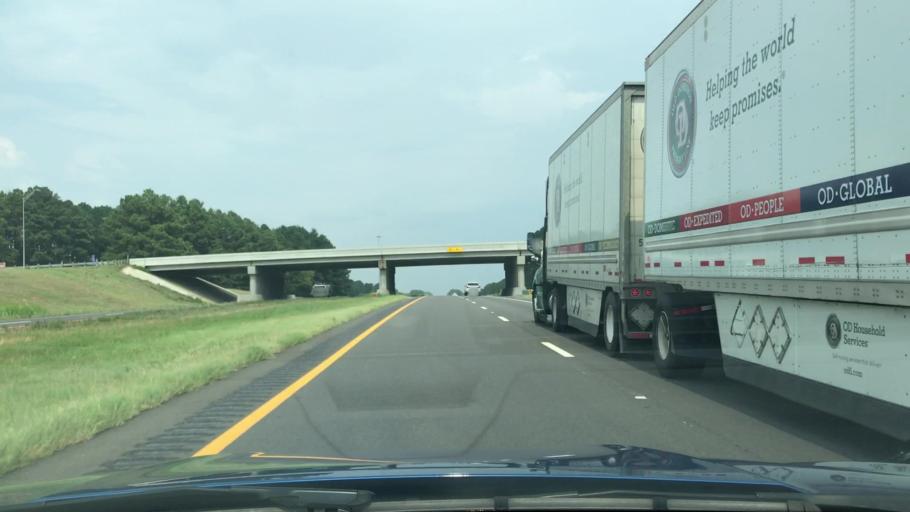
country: US
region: Texas
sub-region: Harrison County
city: Hallsville
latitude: 32.4732
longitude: -94.5811
